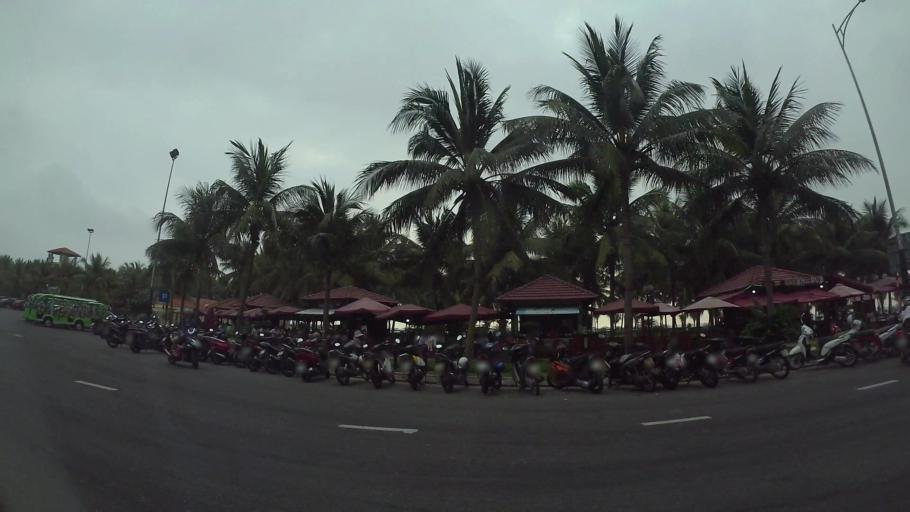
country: VN
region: Da Nang
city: Son Tra
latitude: 16.0723
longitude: 108.2453
